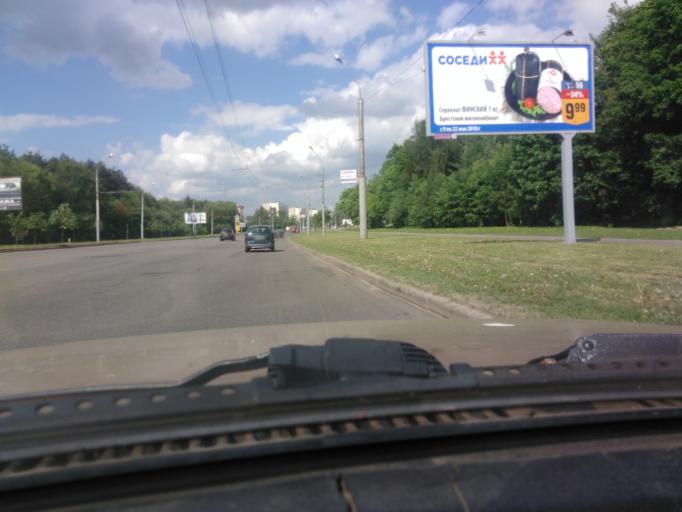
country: BY
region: Mogilev
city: Mahilyow
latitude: 53.9443
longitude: 30.3554
